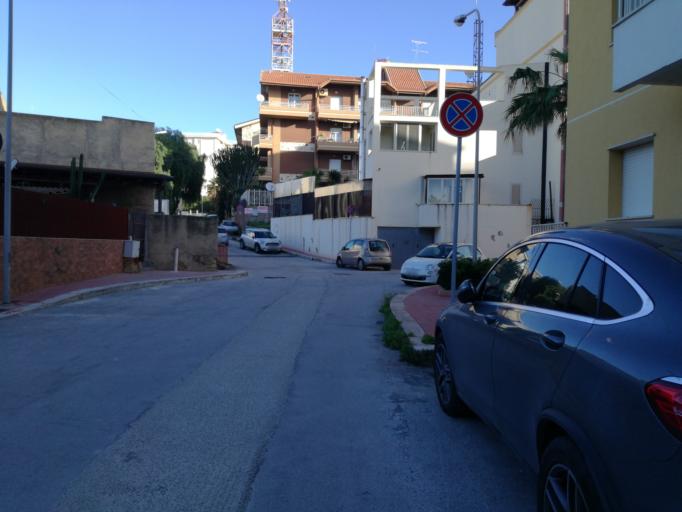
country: IT
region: Sicily
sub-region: Provincia di Caltanissetta
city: Gela
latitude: 37.0737
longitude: 14.2258
